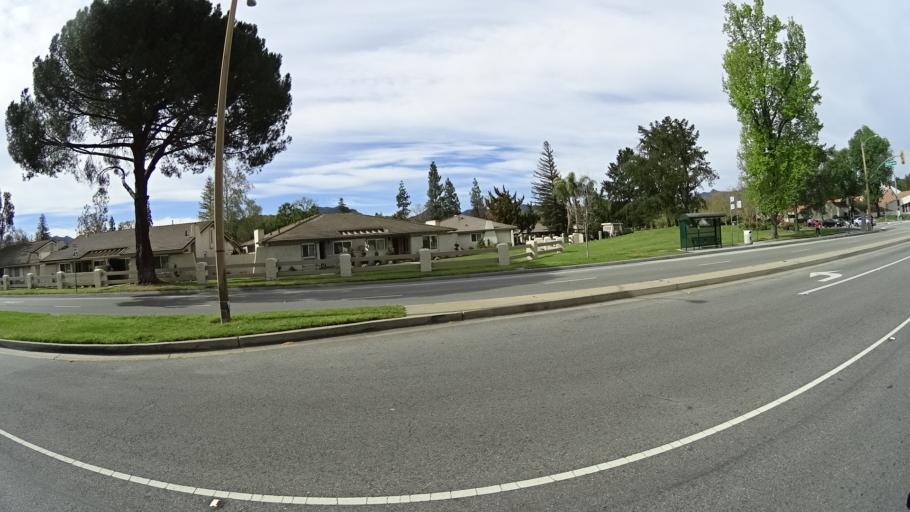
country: US
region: California
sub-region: Ventura County
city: Thousand Oaks
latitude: 34.1519
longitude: -118.8282
